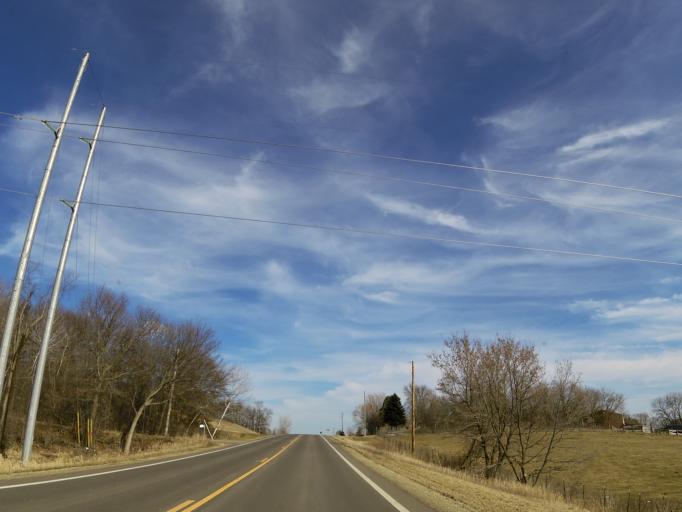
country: US
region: Minnesota
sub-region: Scott County
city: Elko New Market
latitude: 44.5440
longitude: -93.2922
